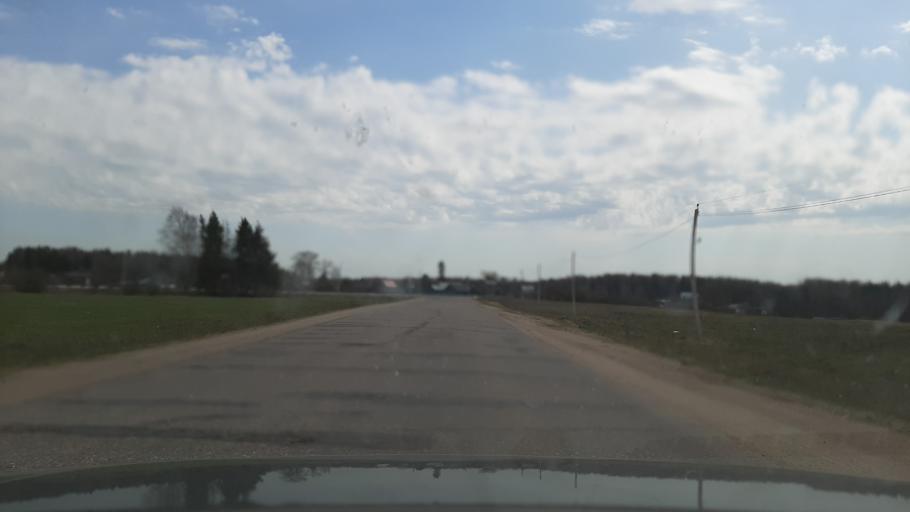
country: RU
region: Ivanovo
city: Furmanov
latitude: 57.1661
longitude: 41.0681
